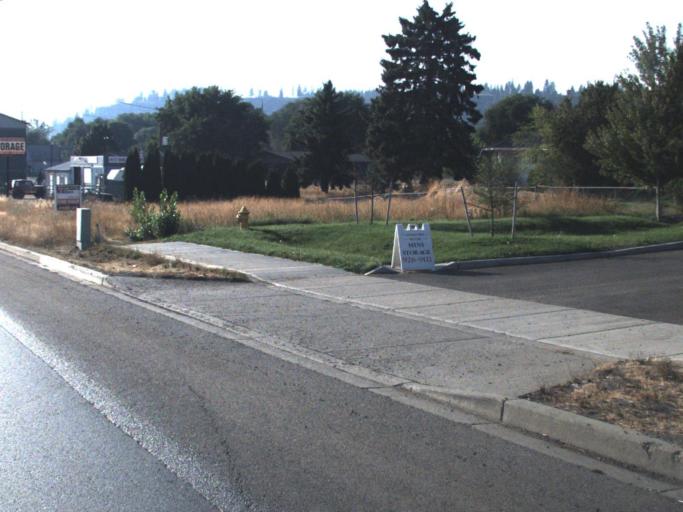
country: US
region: Washington
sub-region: Spokane County
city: Trentwood
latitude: 47.6941
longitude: -117.2263
